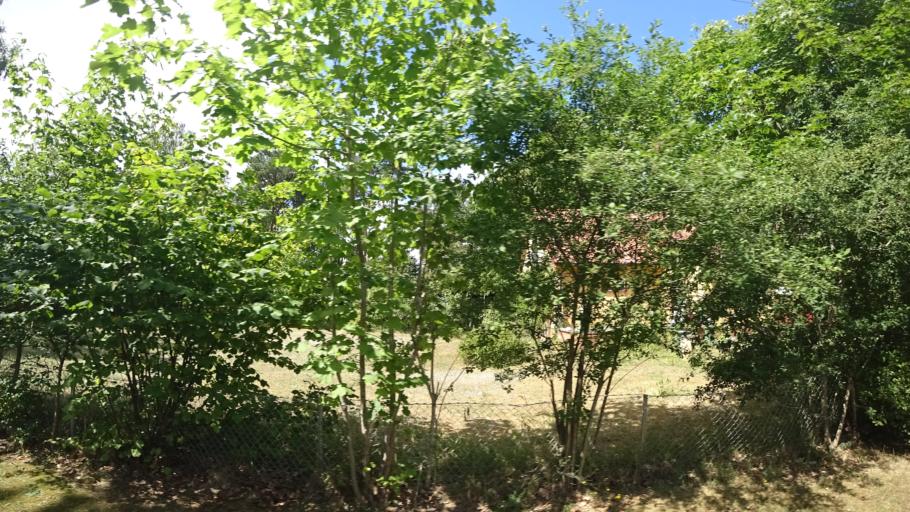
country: SE
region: Skane
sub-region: Kristianstads Kommun
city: Ahus
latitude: 55.9612
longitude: 14.2832
